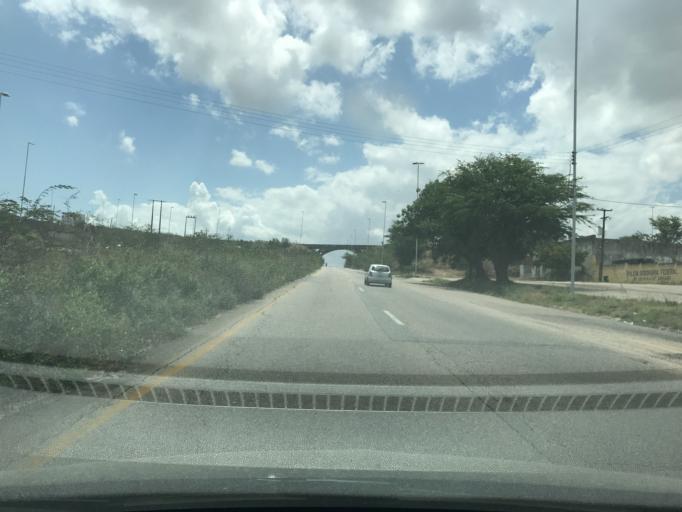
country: BR
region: Pernambuco
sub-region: Caruaru
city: Caruaru
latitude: -8.3068
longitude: -35.9625
